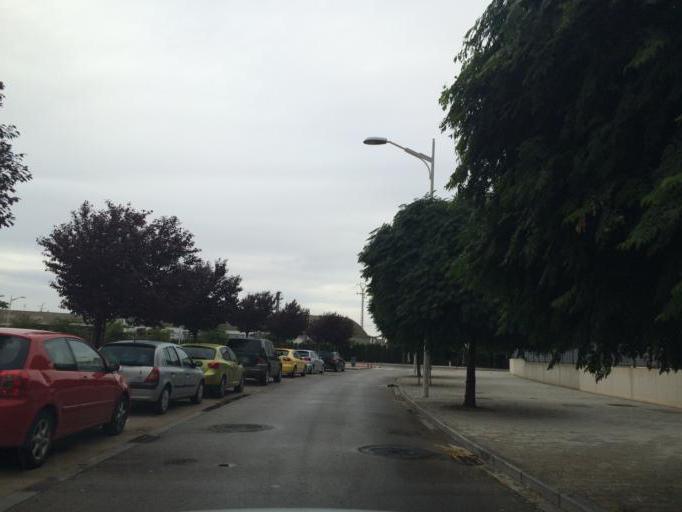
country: ES
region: Castille-La Mancha
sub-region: Provincia de Albacete
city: Albacete
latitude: 39.0094
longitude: -1.8597
